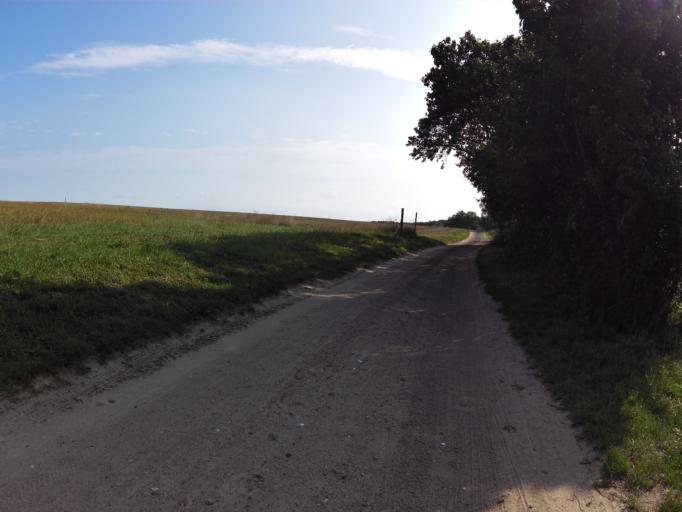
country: DE
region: Mecklenburg-Vorpommern
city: Seebad Bansin
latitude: 53.9538
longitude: 14.1423
